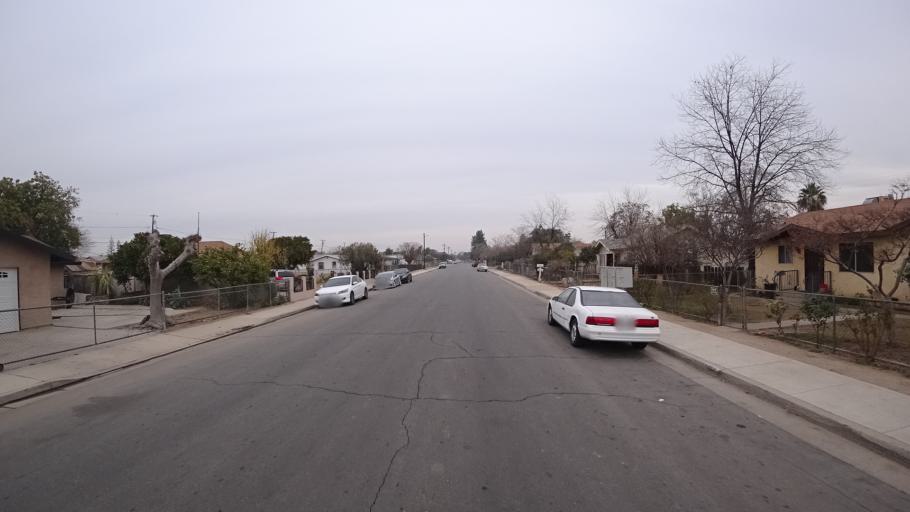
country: US
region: California
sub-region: Kern County
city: Bakersfield
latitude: 35.3665
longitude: -118.9981
